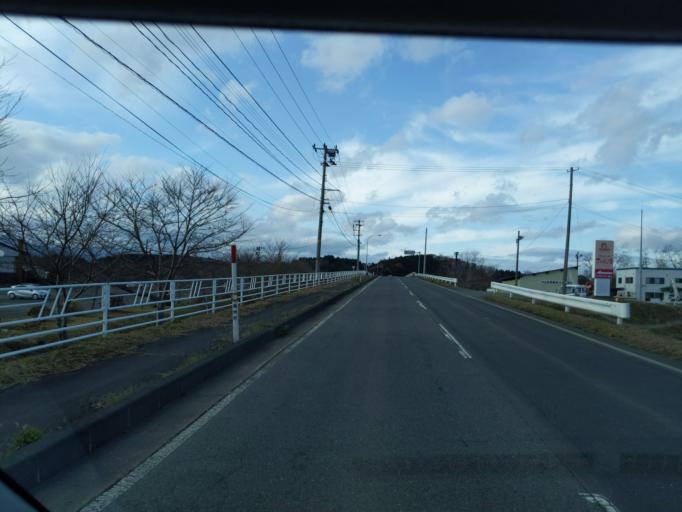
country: JP
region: Iwate
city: Mizusawa
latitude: 39.1644
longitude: 141.0919
